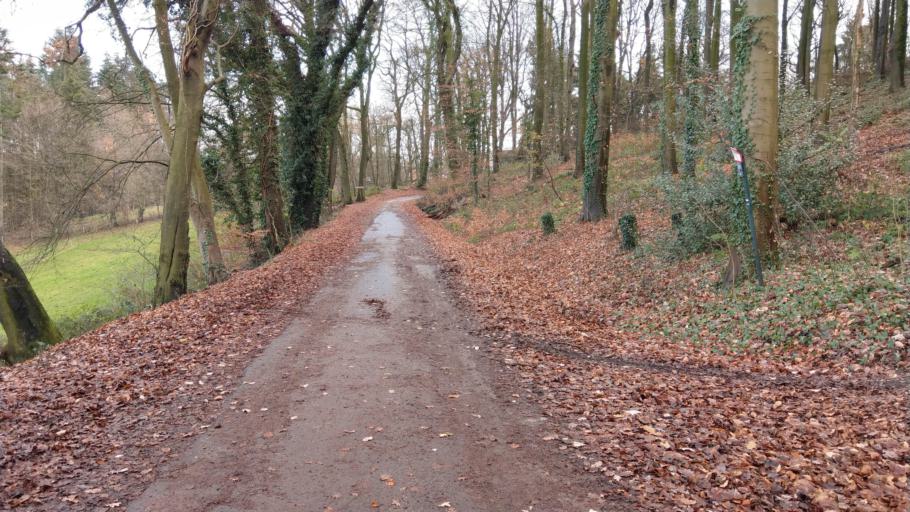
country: DE
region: North Rhine-Westphalia
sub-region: Regierungsbezirk Koln
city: Aachen
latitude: 50.7501
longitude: 6.0555
